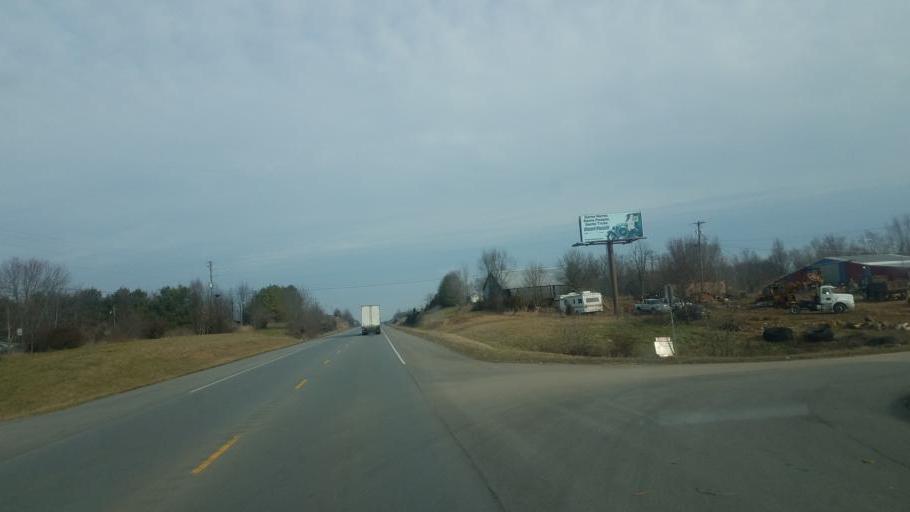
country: US
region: Kentucky
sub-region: Boyle County
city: Junction City
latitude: 37.5419
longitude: -84.8028
